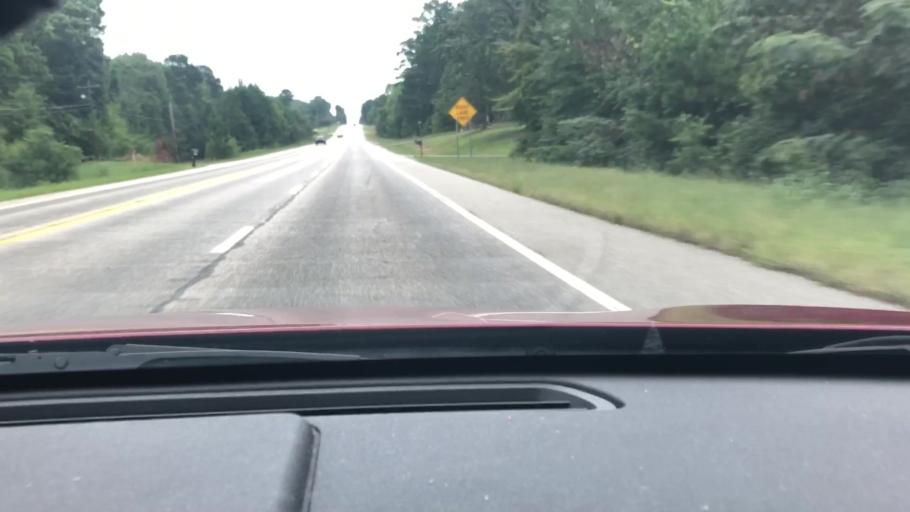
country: US
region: Arkansas
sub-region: Miller County
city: Texarkana
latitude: 33.4295
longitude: -93.9479
